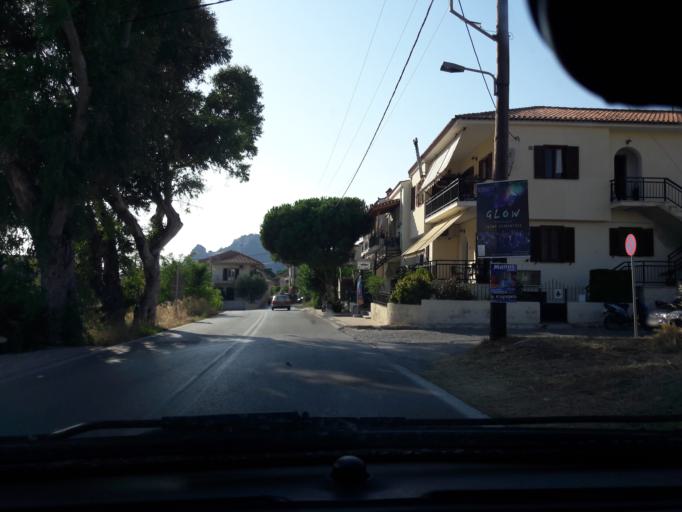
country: GR
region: North Aegean
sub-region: Nomos Lesvou
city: Myrina
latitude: 39.8717
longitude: 25.0672
